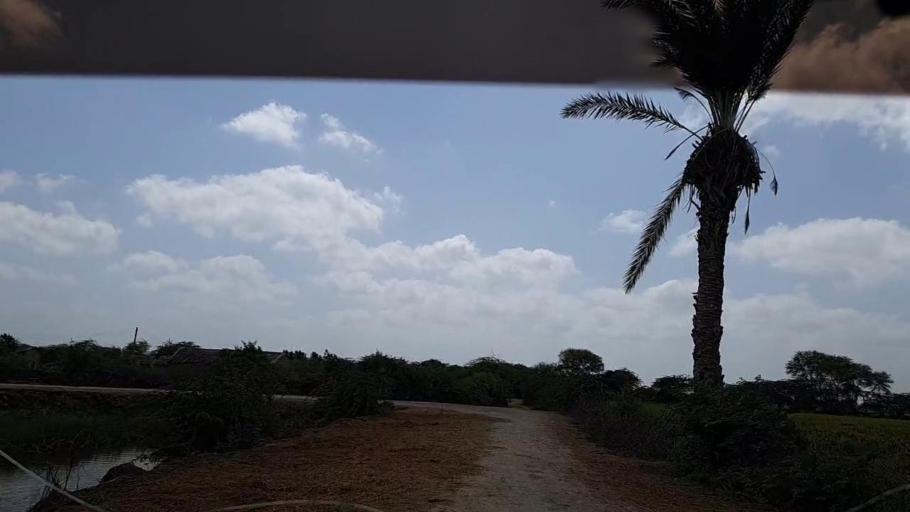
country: PK
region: Sindh
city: Badin
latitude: 24.5834
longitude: 68.7656
